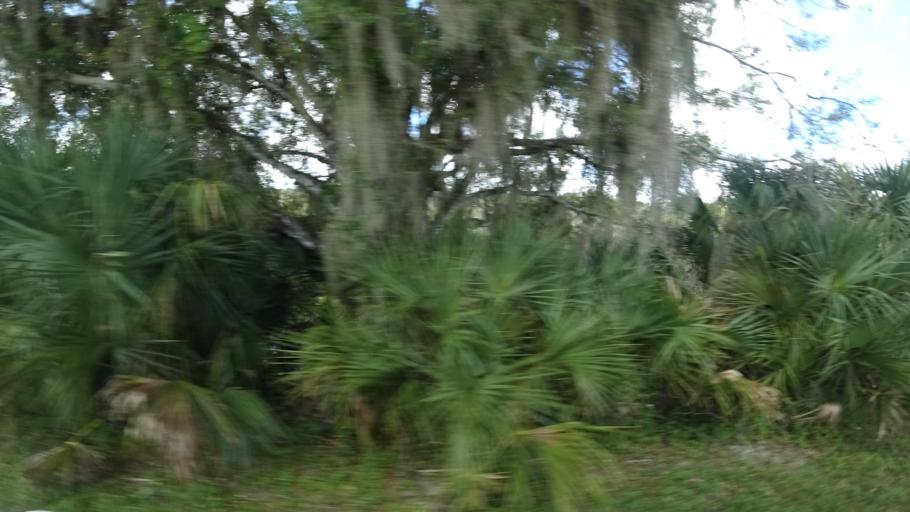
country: US
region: Florida
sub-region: Sarasota County
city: Lake Sarasota
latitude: 27.2964
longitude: -82.2530
